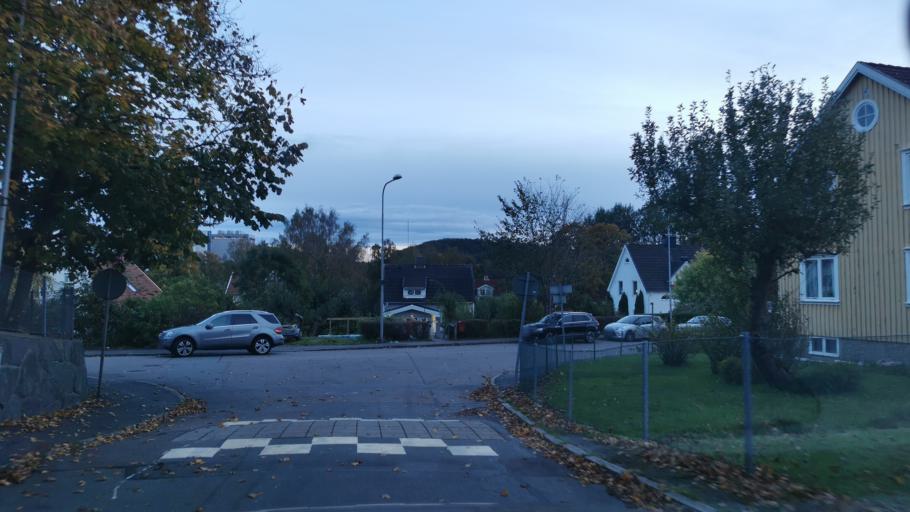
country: SE
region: Vaestra Goetaland
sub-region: Goteborg
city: Eriksbo
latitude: 57.7365
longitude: 12.0483
